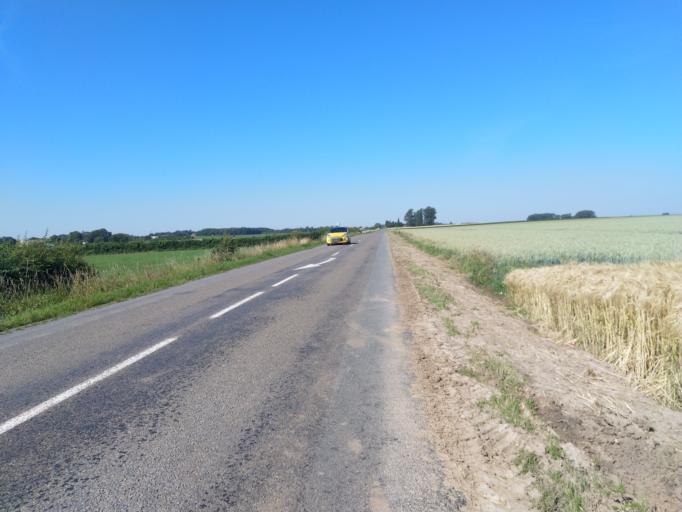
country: FR
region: Nord-Pas-de-Calais
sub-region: Departement du Nord
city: La Longueville
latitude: 50.3073
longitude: 3.8316
